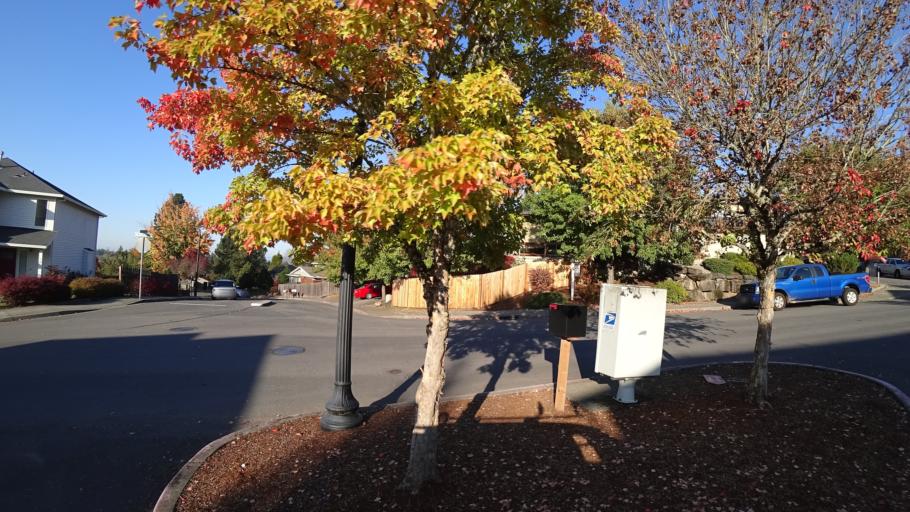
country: US
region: Oregon
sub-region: Multnomah County
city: Gresham
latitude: 45.4812
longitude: -122.4469
